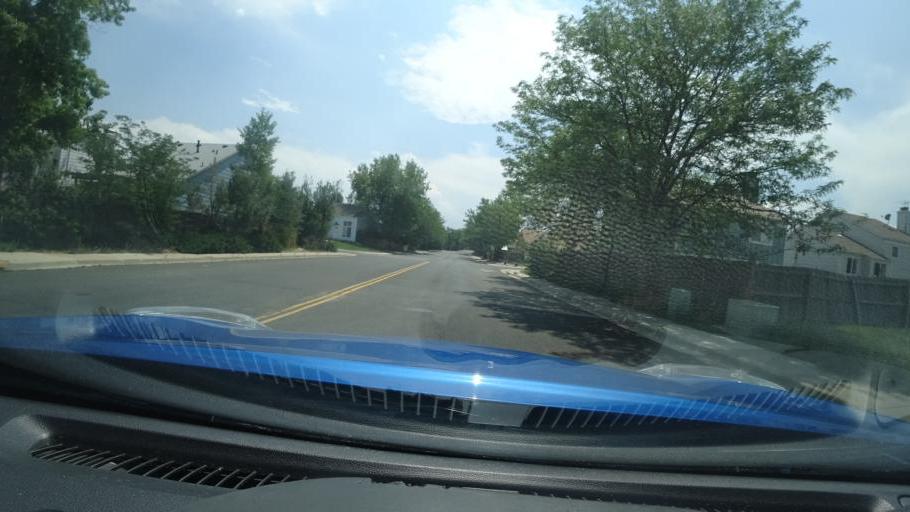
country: US
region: Colorado
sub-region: Adams County
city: Aurora
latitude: 39.6676
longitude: -104.7591
